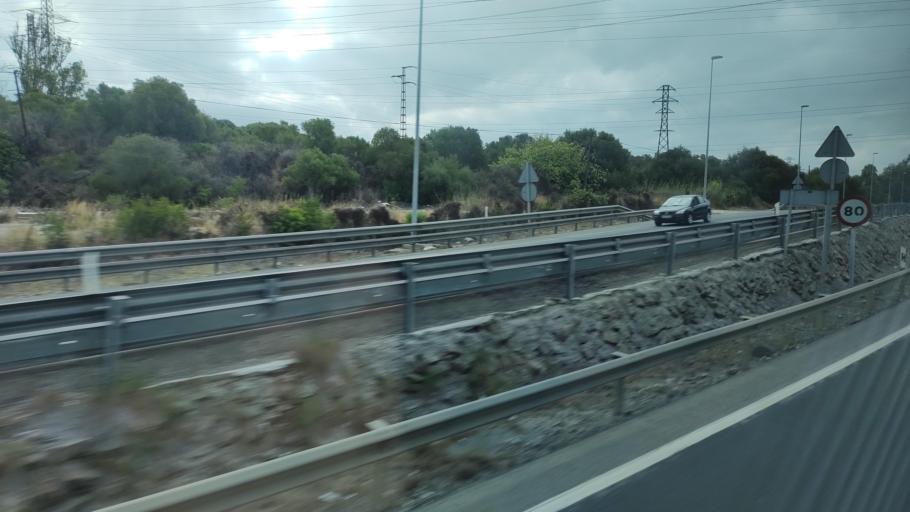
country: ES
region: Andalusia
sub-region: Provincia de Cadiz
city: San Roque
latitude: 36.1886
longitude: -5.3859
